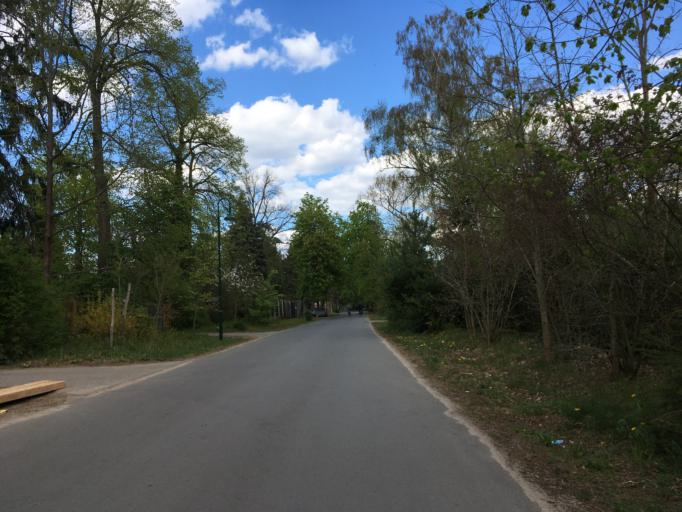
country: DE
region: Brandenburg
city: Wandlitz
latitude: 52.7734
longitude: 13.4417
